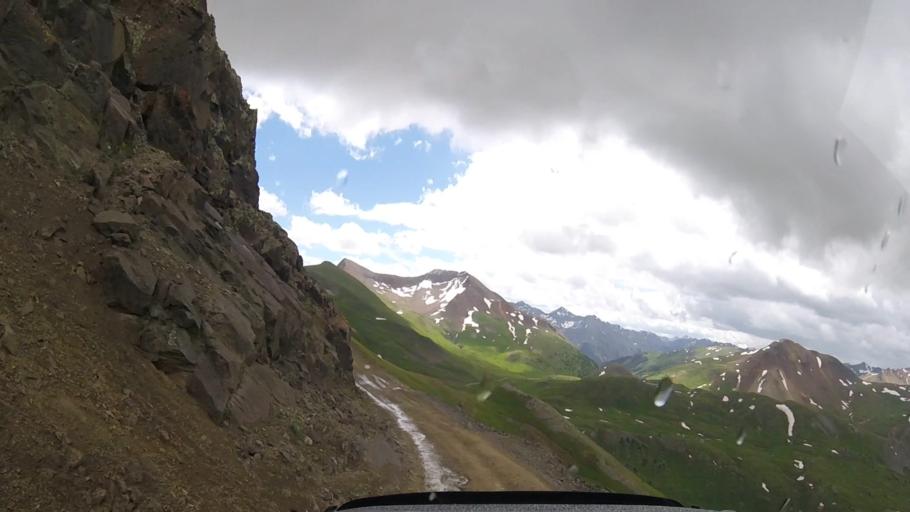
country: US
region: Colorado
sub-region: Ouray County
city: Ouray
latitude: 37.9663
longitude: -107.5851
